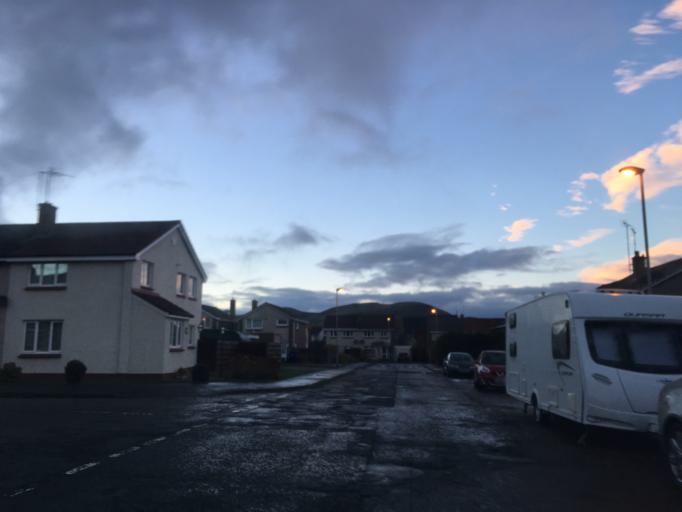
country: GB
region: Scotland
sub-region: Midlothian
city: Loanhead
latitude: 55.8569
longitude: -3.1732
